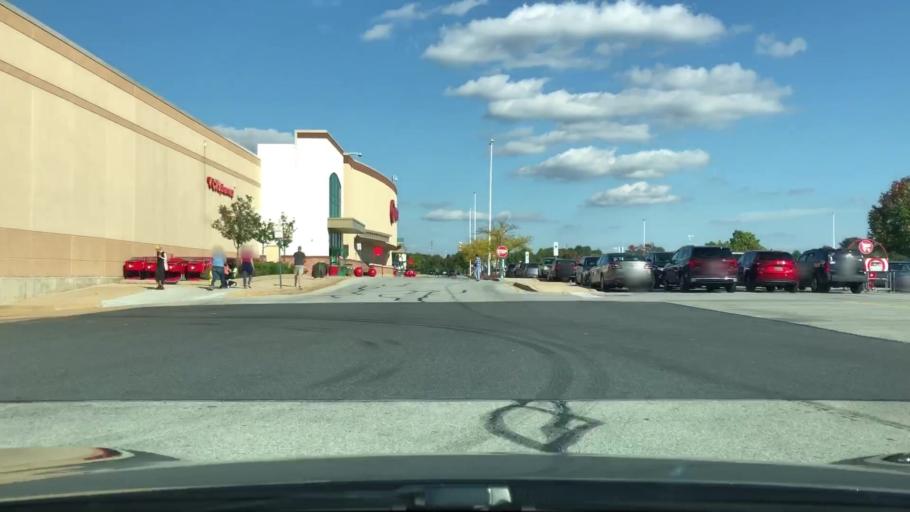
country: US
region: Delaware
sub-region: New Castle County
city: Bellefonte
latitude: 39.8306
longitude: -75.5415
